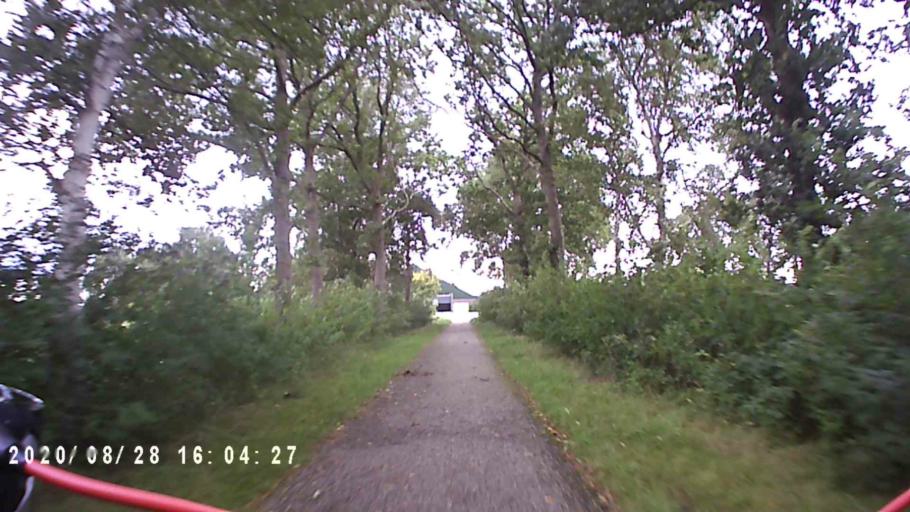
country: NL
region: Drenthe
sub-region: Gemeente Tynaarlo
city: Vries
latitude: 53.1141
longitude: 6.4969
